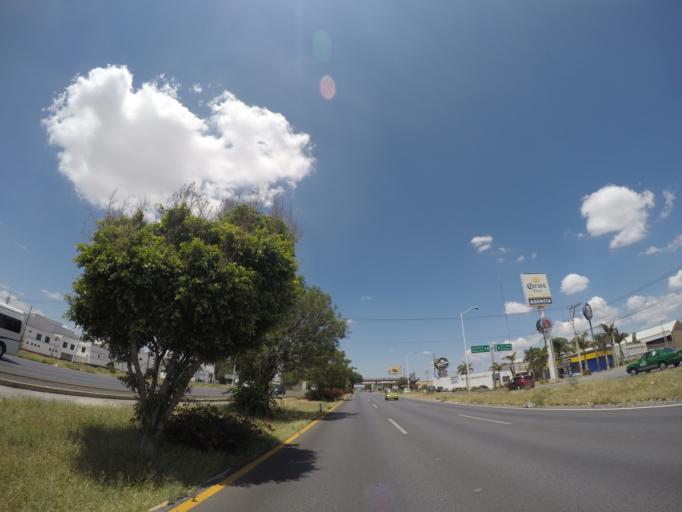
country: MX
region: San Luis Potosi
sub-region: Soledad de Graciano Sanchez
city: Soledad de Graciano Sanchez
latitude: 22.1245
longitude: -100.9170
